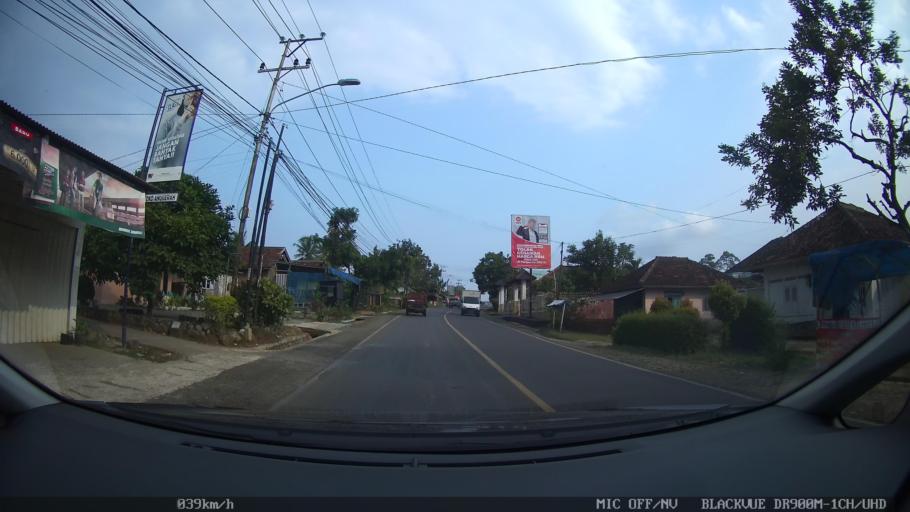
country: ID
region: Lampung
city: Natar
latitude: -5.3725
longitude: 105.1933
